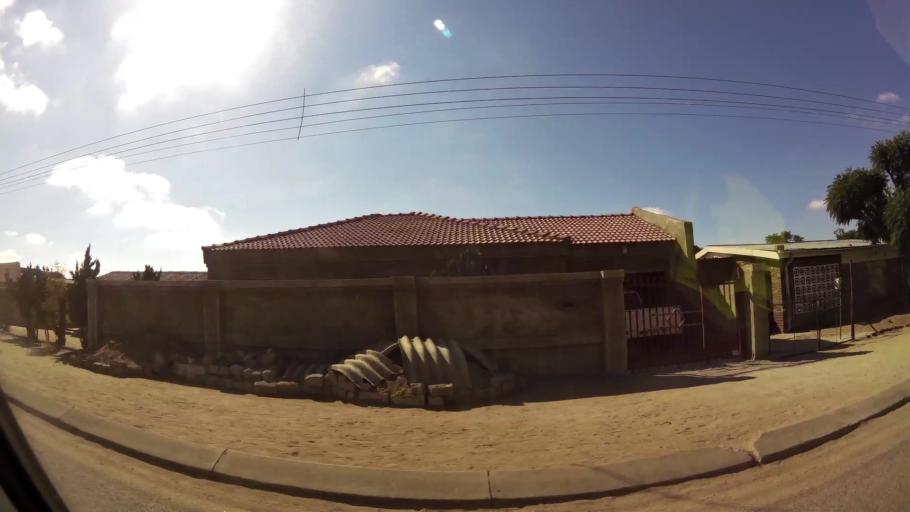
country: ZA
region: Limpopo
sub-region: Capricorn District Municipality
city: Polokwane
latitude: -23.8621
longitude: 29.3901
